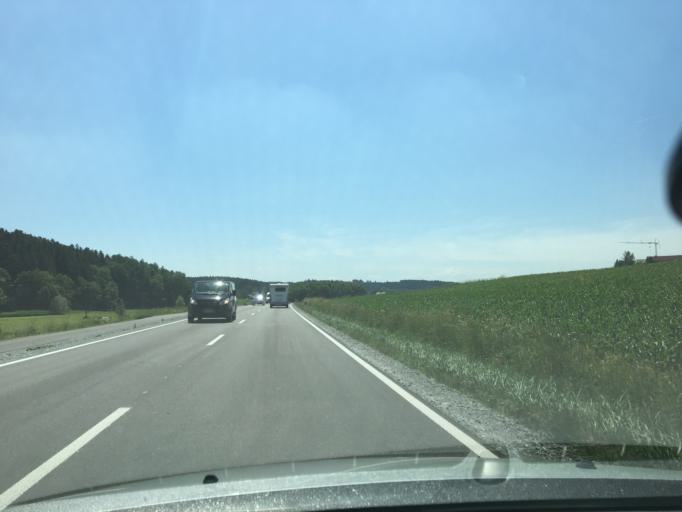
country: DE
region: Bavaria
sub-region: Upper Bavaria
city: Rohrbach
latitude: 48.3109
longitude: 12.5607
